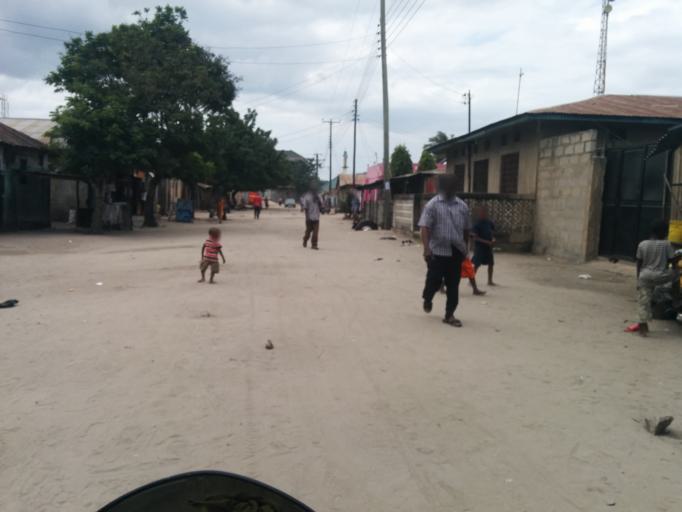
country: TZ
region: Dar es Salaam
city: Dar es Salaam
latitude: -6.8609
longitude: 39.2550
